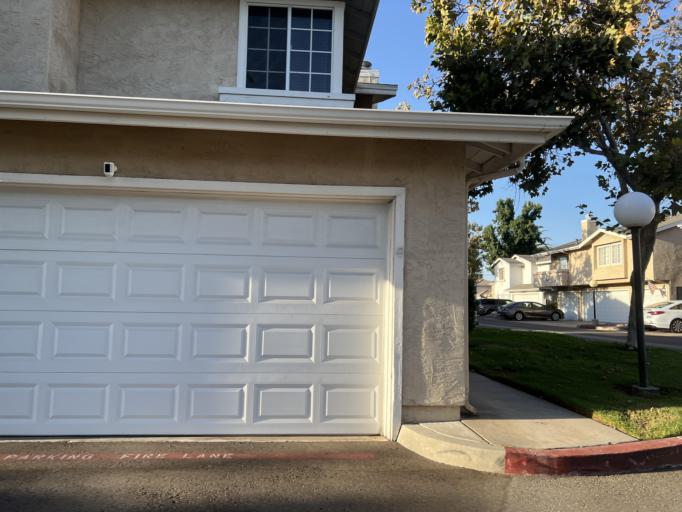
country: US
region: California
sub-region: San Diego County
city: Bostonia
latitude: 32.7920
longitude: -116.9286
